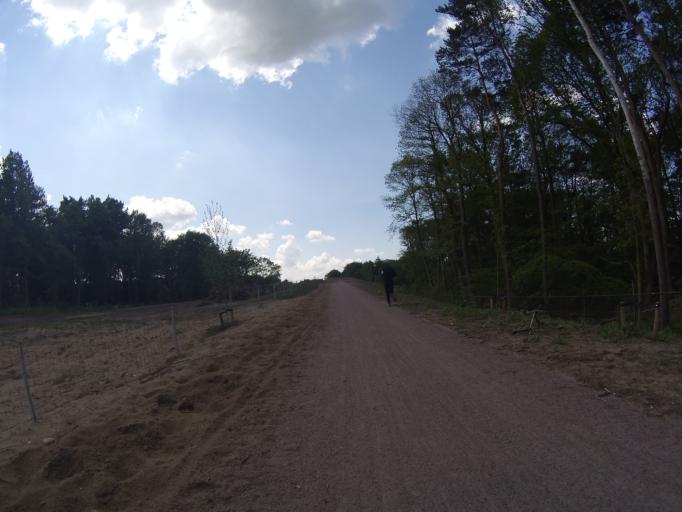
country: NL
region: North Holland
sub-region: Gemeente Laren
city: Laren
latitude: 52.2674
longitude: 5.2104
